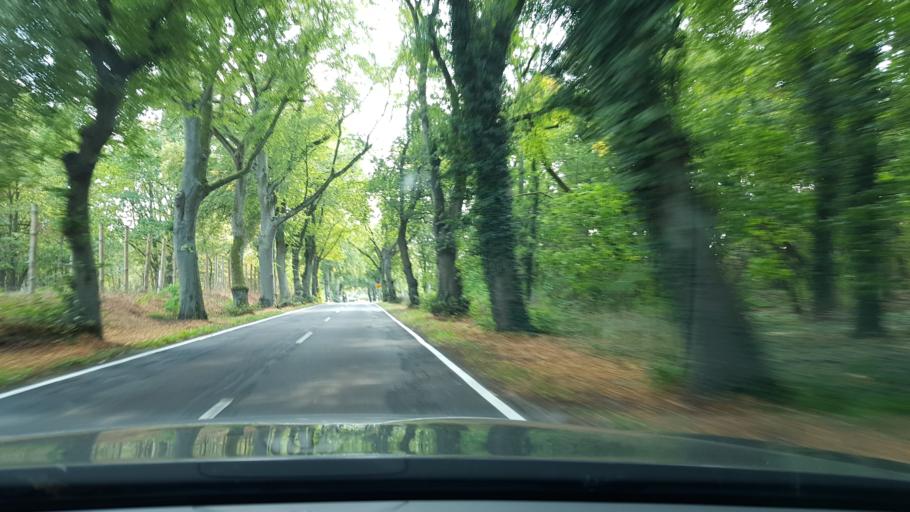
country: DE
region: Brandenburg
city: Lindow
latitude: 52.9796
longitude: 12.9837
